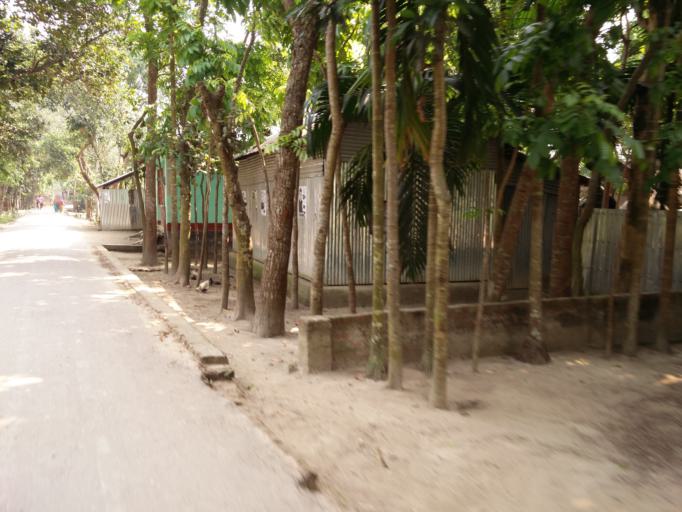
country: BD
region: Dhaka
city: Muktagacha
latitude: 24.9139
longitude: 90.2165
